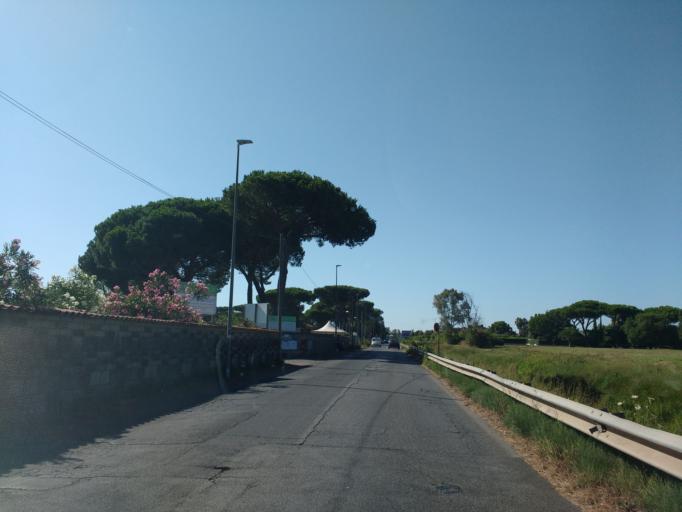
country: IT
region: Latium
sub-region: Citta metropolitana di Roma Capitale
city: Acilia-Castel Fusano-Ostia Antica
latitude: 41.7434
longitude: 12.3379
